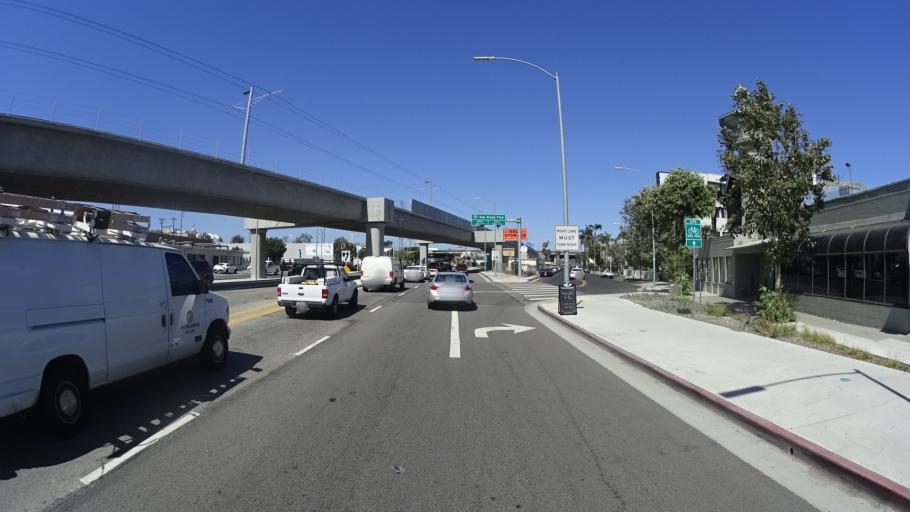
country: US
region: California
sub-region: Los Angeles County
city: Westwood, Los Angeles
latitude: 34.0338
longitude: -118.4414
